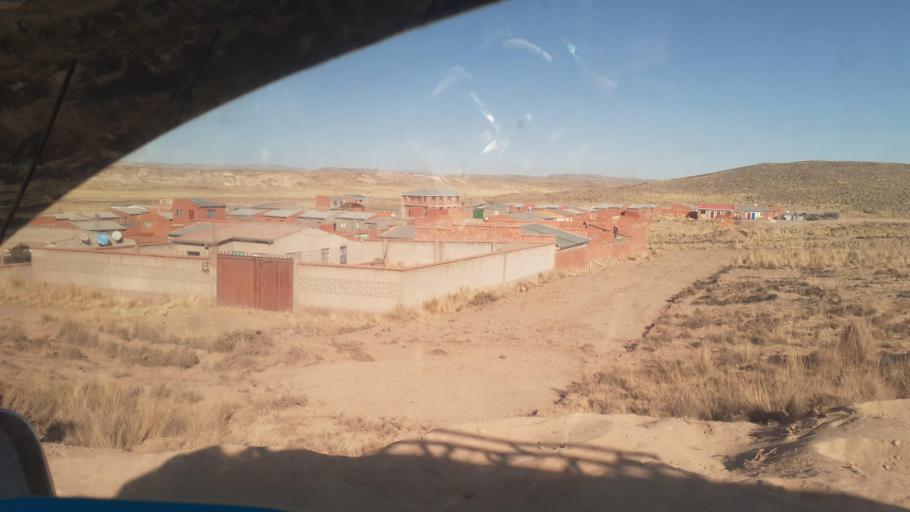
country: BO
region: La Paz
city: Tiahuanaco
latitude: -17.1123
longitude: -68.7786
